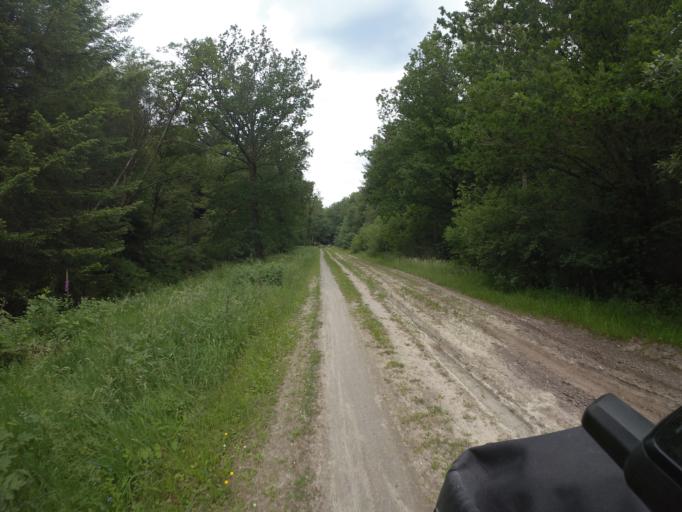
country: NL
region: Drenthe
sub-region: Gemeente Assen
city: Assen
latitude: 53.0185
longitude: 6.4166
